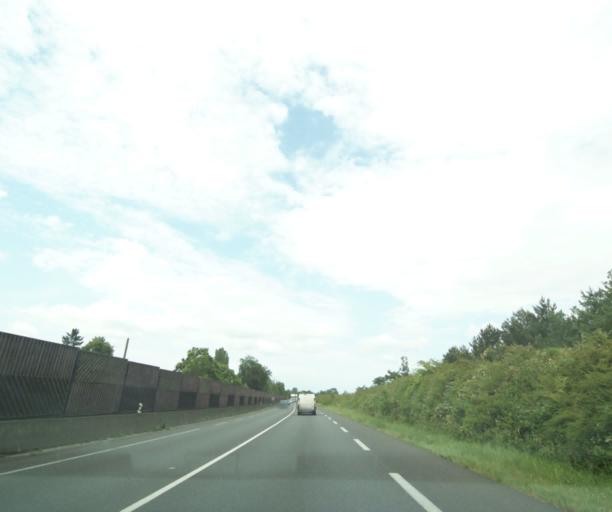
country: FR
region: Pays de la Loire
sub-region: Departement de Maine-et-Loire
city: Saumur
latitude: 47.2572
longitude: -0.0981
